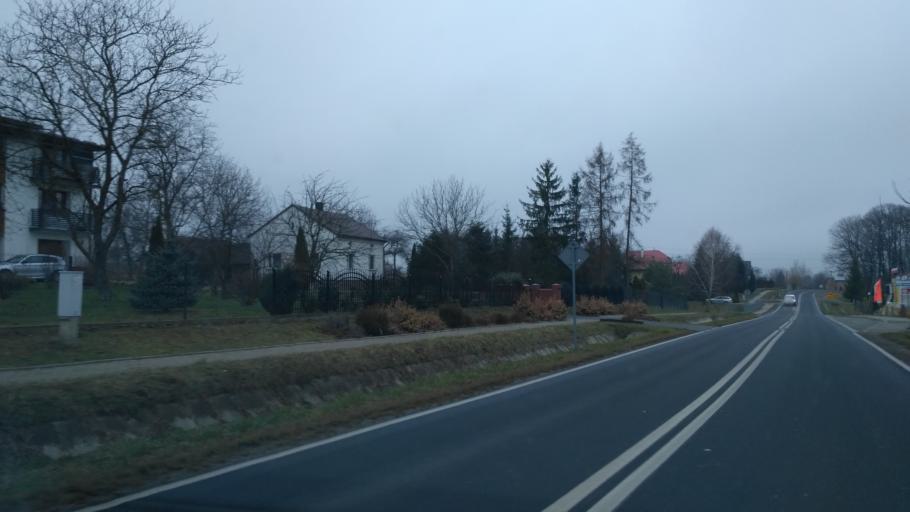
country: PL
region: Subcarpathian Voivodeship
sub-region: Powiat jaroslawski
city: Pruchnik
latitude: 49.9184
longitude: 22.5665
